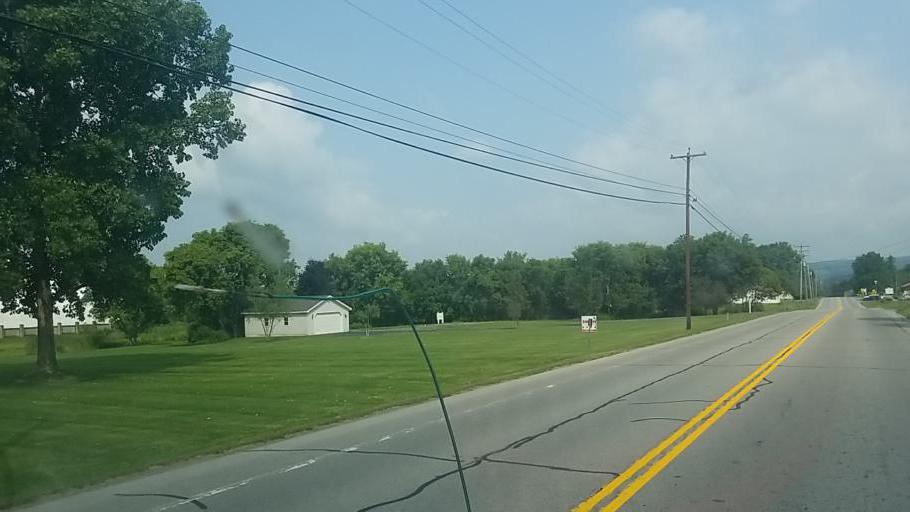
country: US
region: New York
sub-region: Montgomery County
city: Fort Plain
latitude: 42.9497
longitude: -74.6201
